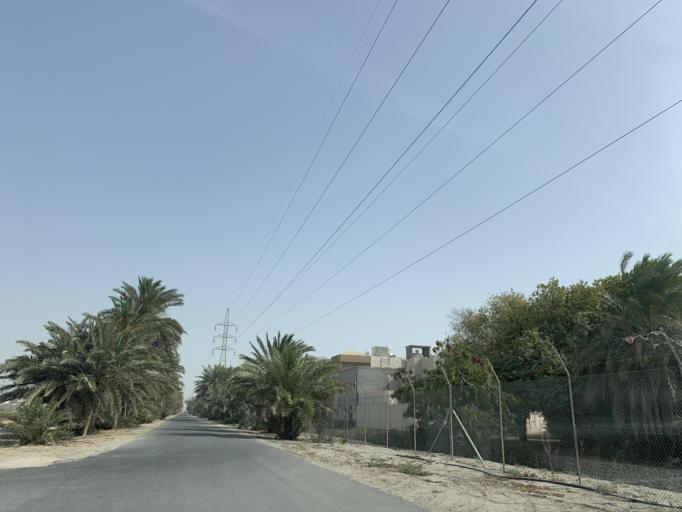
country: BH
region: Northern
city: Madinat `Isa
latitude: 26.1695
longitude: 50.5359
